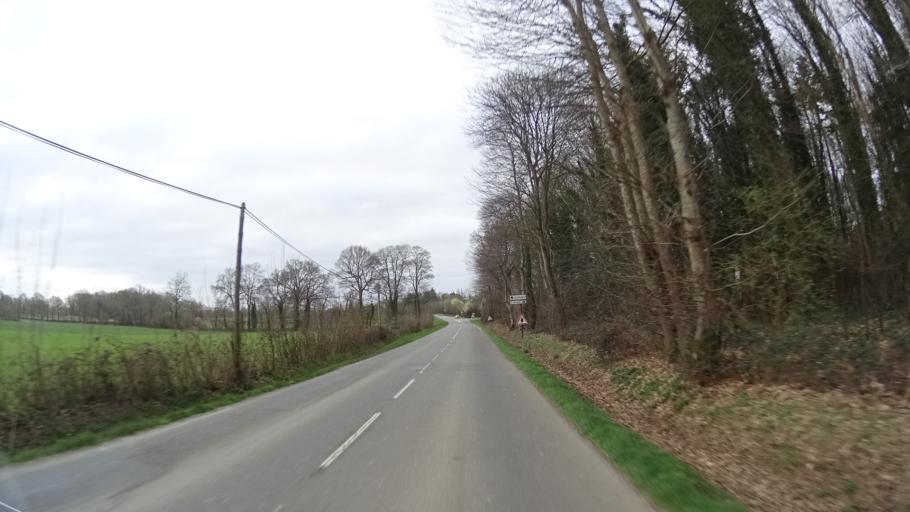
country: FR
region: Brittany
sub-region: Departement d'Ille-et-Vilaine
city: Saint-Gilles
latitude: 48.1762
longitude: -1.8472
